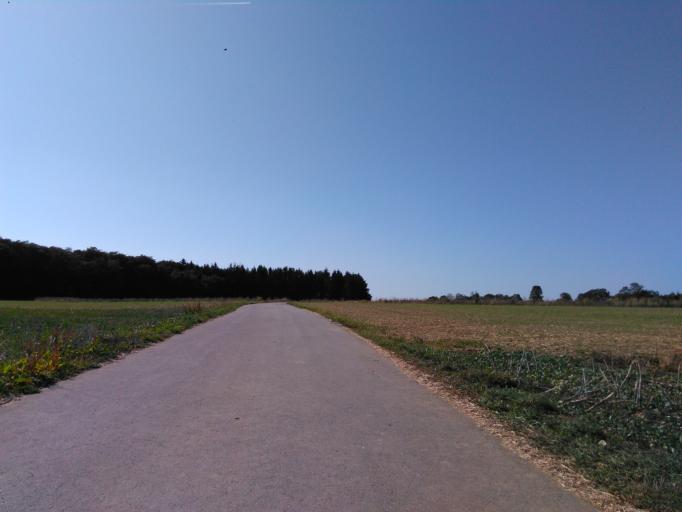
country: LU
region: Diekirch
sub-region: Canton de Redange
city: Rambrouch
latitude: 49.8384
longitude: 5.7977
